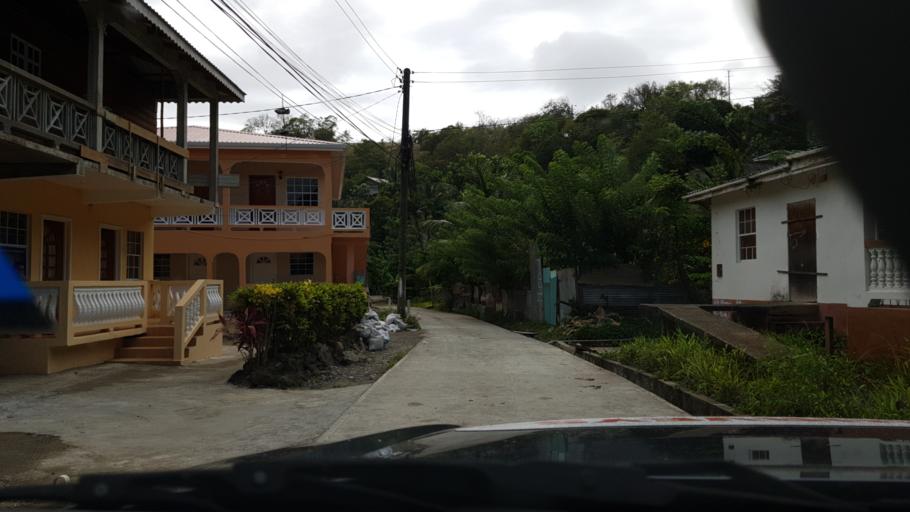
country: LC
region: Anse-la-Raye
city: Anse La Raye
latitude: 13.9428
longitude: -61.0414
